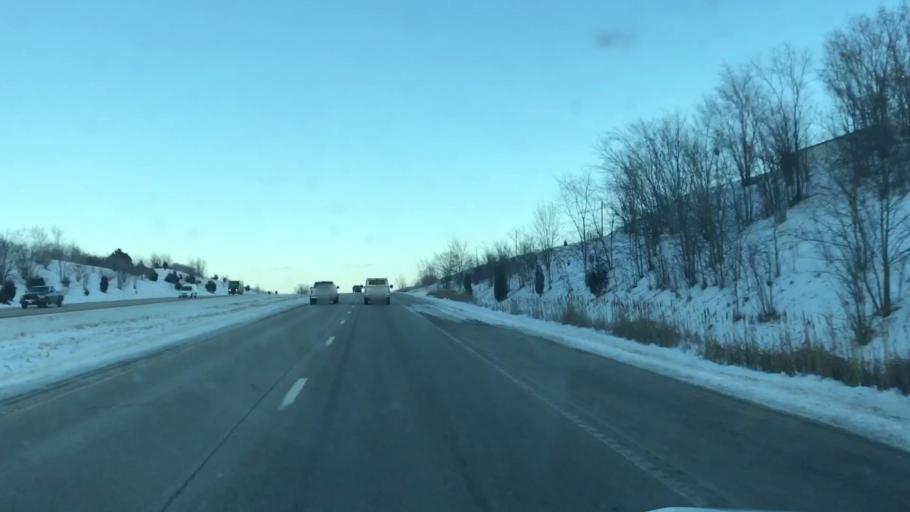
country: US
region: Missouri
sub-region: Buchanan County
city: Saint Joseph
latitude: 39.7476
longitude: -94.7089
